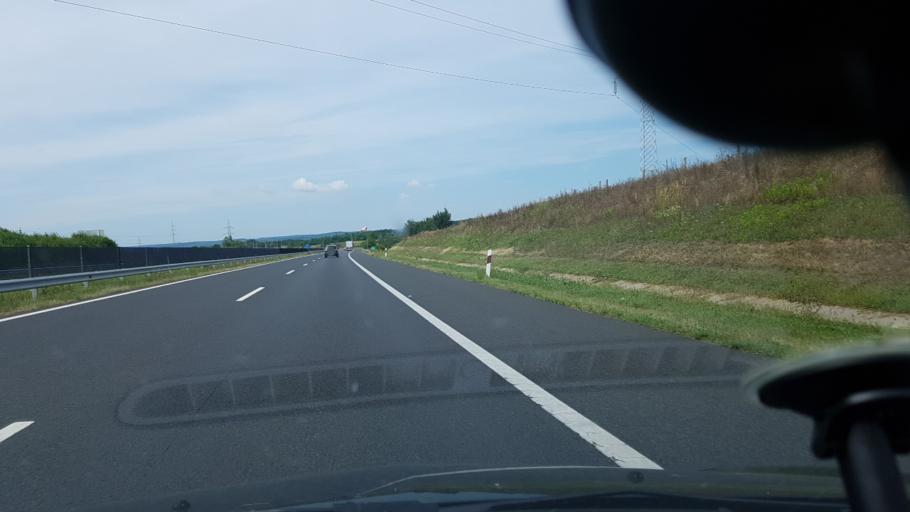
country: HU
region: Zala
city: Nagykanizsa
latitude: 46.4769
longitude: 17.0078
